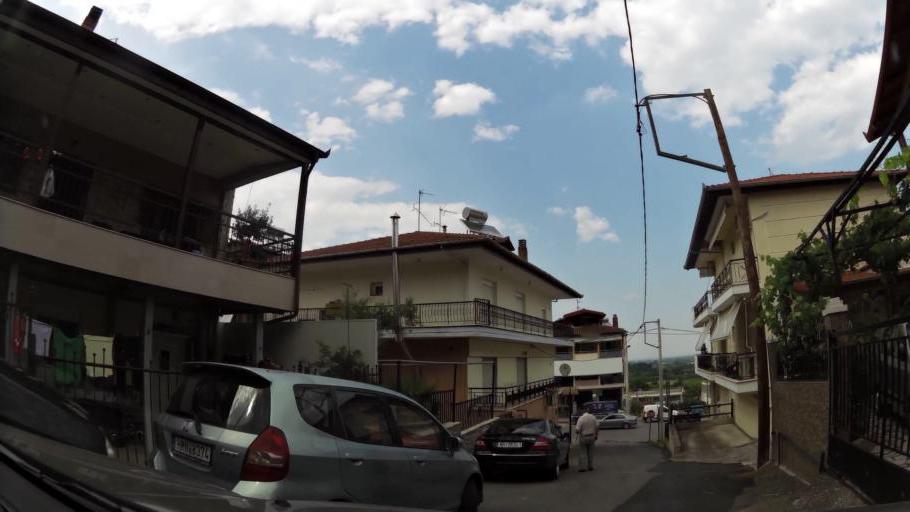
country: GR
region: Central Macedonia
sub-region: Nomos Imathias
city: Veroia
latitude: 40.5113
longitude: 22.2134
